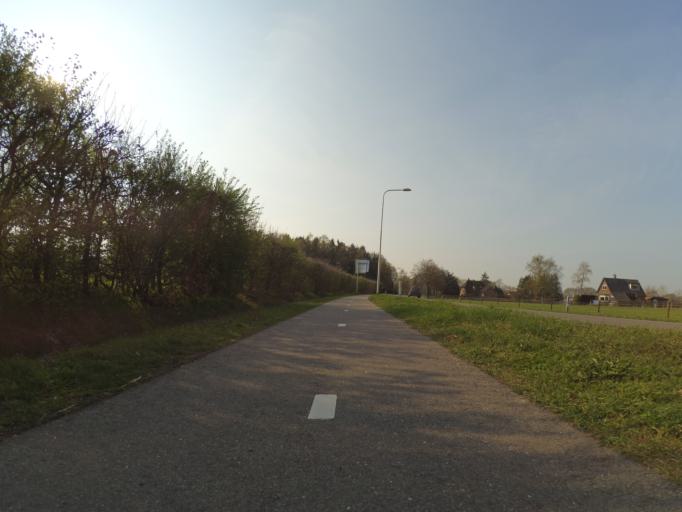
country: NL
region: Gelderland
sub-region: Gemeente Putten
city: Putten
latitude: 52.2368
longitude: 5.6098
